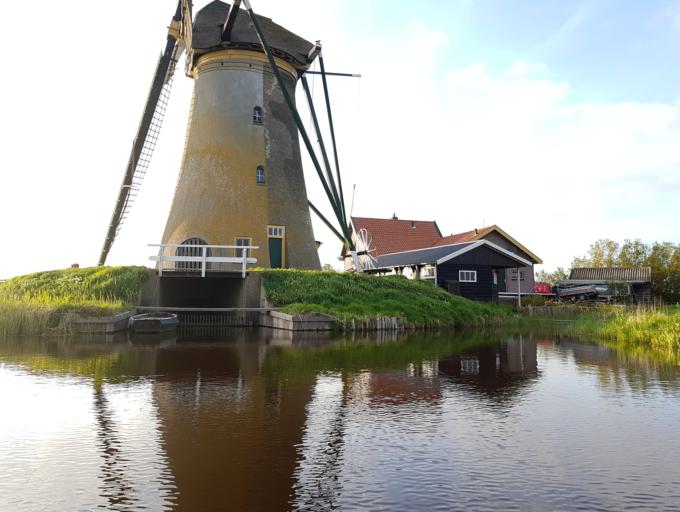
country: NL
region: South Holland
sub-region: Gemeente Leiderdorp
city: Leiderdorp
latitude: 52.1860
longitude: 4.5244
